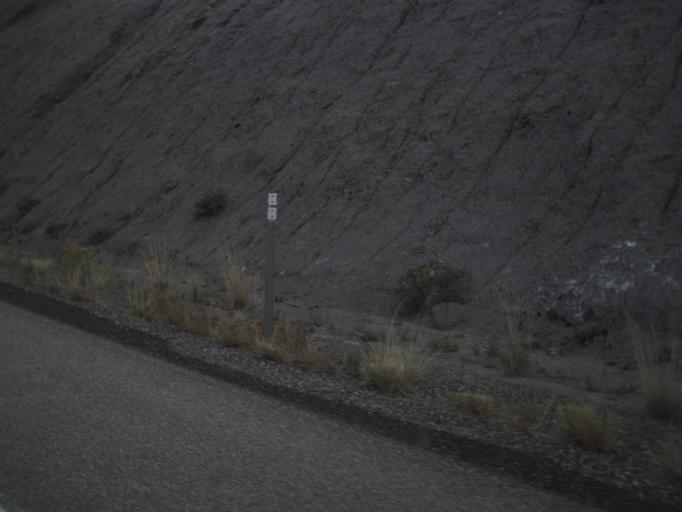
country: US
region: Utah
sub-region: Emery County
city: Ferron
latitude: 38.7666
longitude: -111.3449
